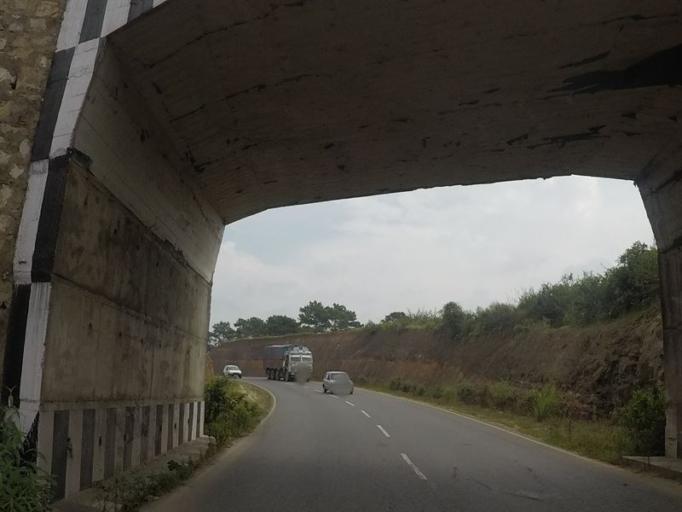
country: IN
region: Meghalaya
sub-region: East Khasi Hills
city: Shillong
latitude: 25.4909
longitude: 92.1807
